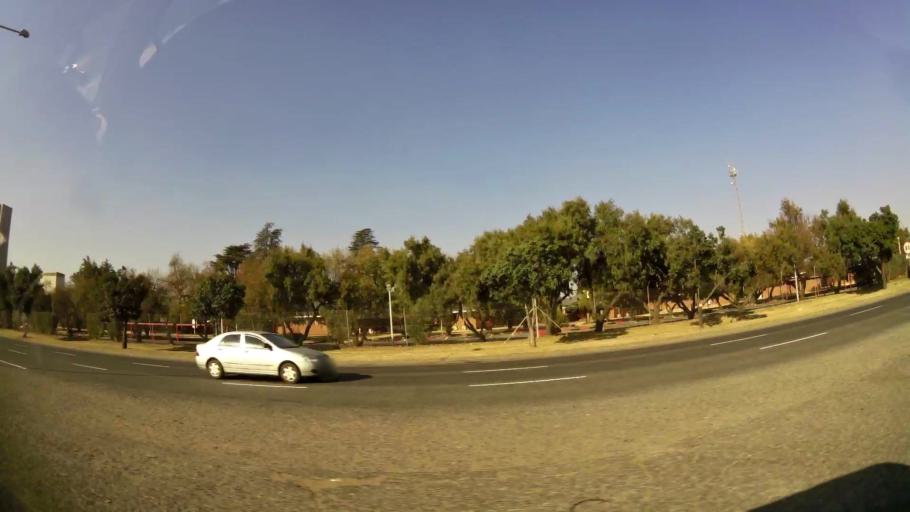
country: ZA
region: Gauteng
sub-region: West Rand District Municipality
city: Randfontein
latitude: -26.1693
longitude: 27.7118
